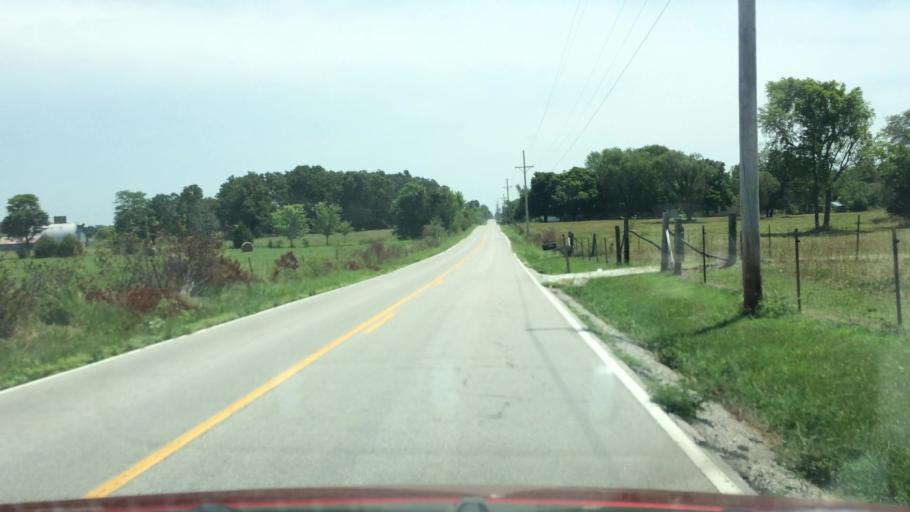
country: US
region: Missouri
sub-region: Greene County
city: Strafford
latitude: 37.2713
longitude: -93.1573
